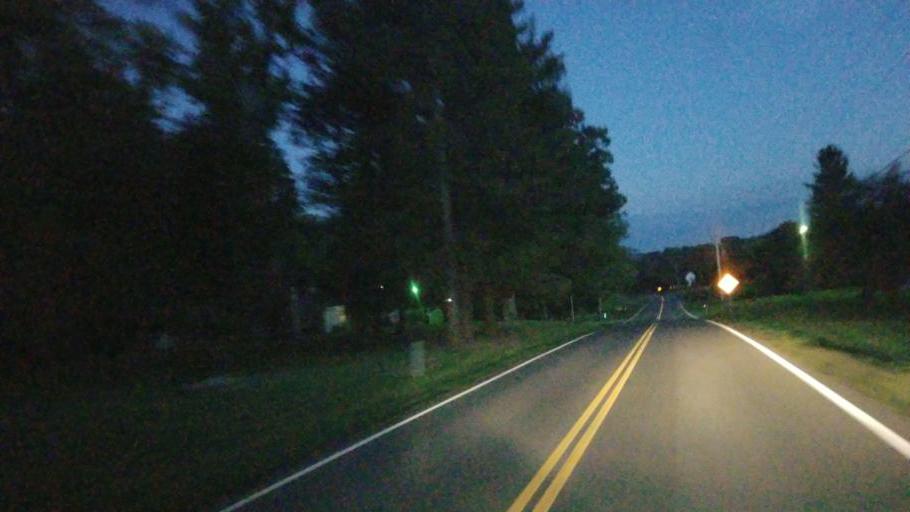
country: US
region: Ohio
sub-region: Ashland County
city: Ashland
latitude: 40.8276
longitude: -82.3982
